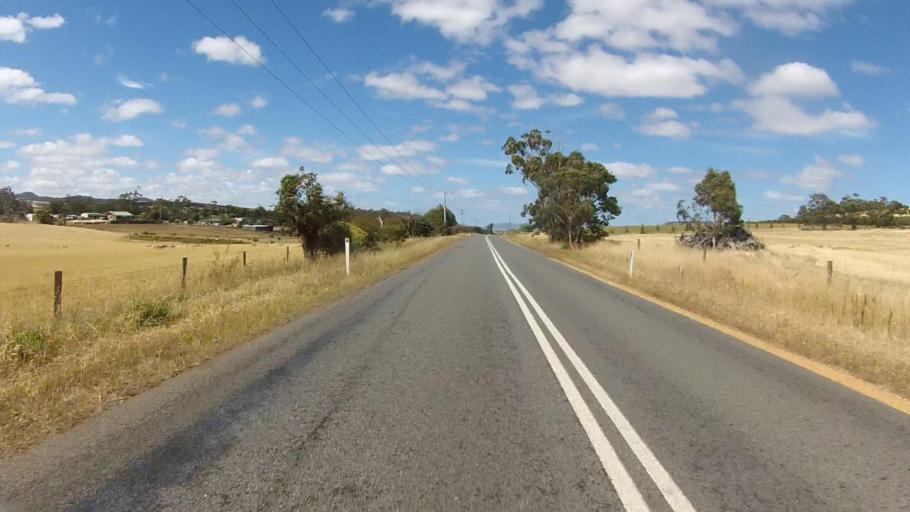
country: AU
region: Tasmania
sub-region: Sorell
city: Sorell
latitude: -42.6417
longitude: 147.4336
